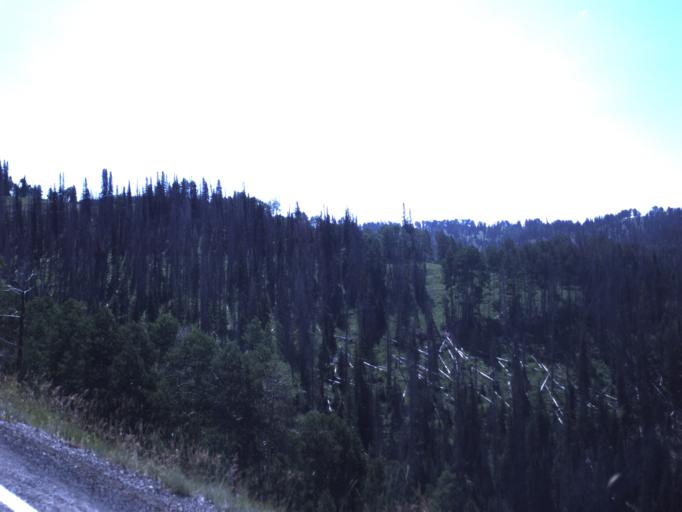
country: US
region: Utah
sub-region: Sanpete County
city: Fairview
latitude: 39.6826
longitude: -111.2372
